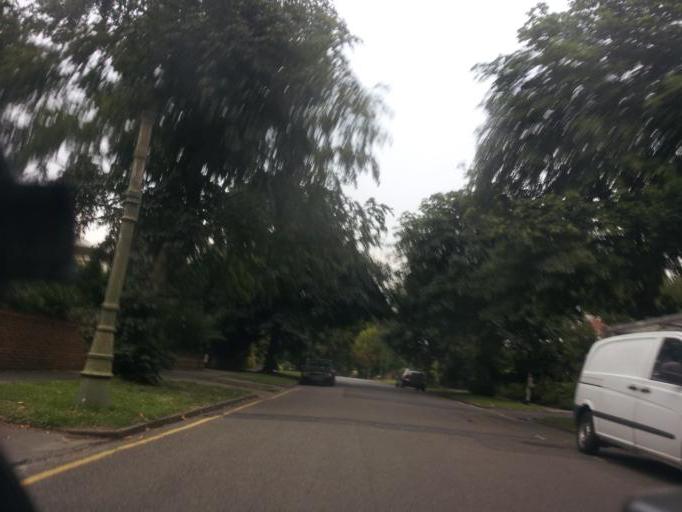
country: GB
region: England
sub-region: Greater London
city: Beckenham
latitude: 51.4147
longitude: -0.0299
